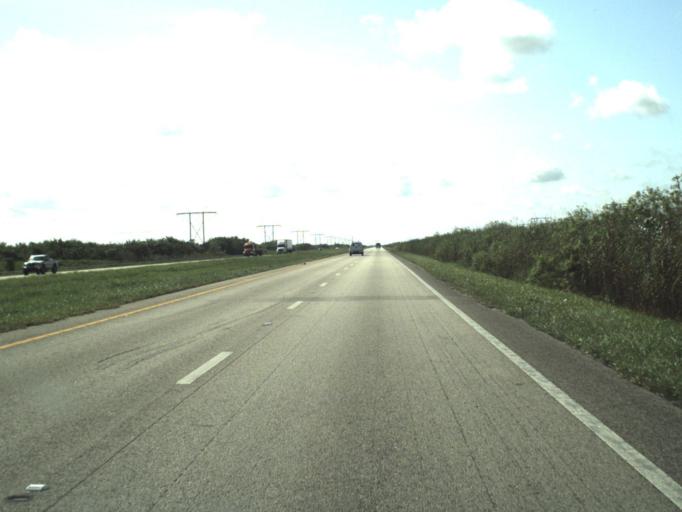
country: US
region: Florida
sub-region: Broward County
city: Weston
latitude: 26.2677
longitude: -80.4862
